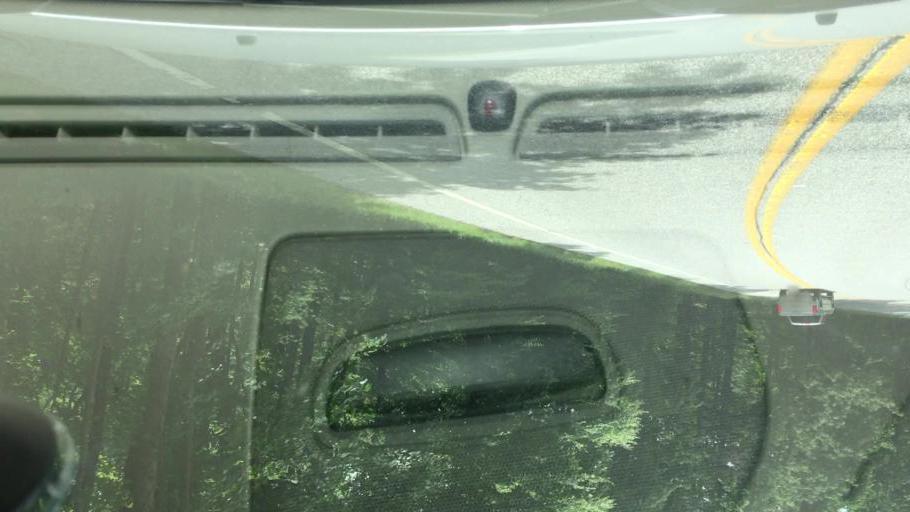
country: US
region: Georgia
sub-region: Union County
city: Blairsville
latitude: 34.7121
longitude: -83.9120
